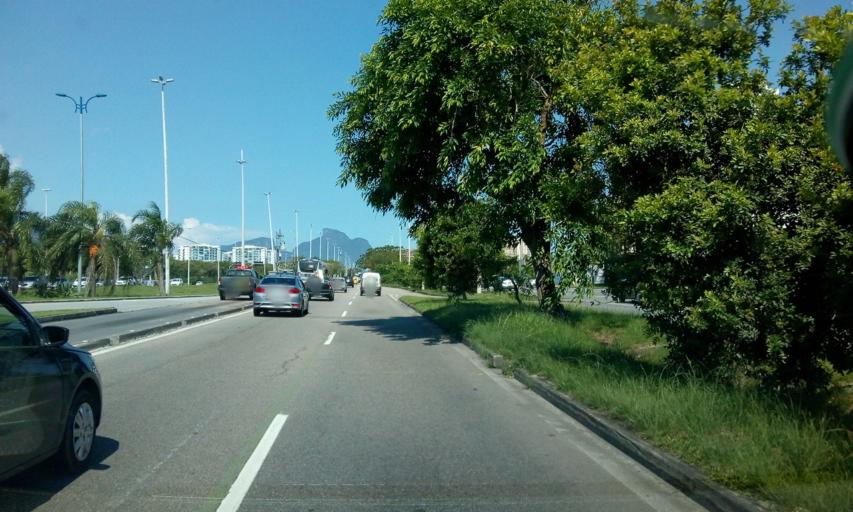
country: BR
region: Rio de Janeiro
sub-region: Nilopolis
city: Nilopolis
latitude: -23.0001
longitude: -43.4068
